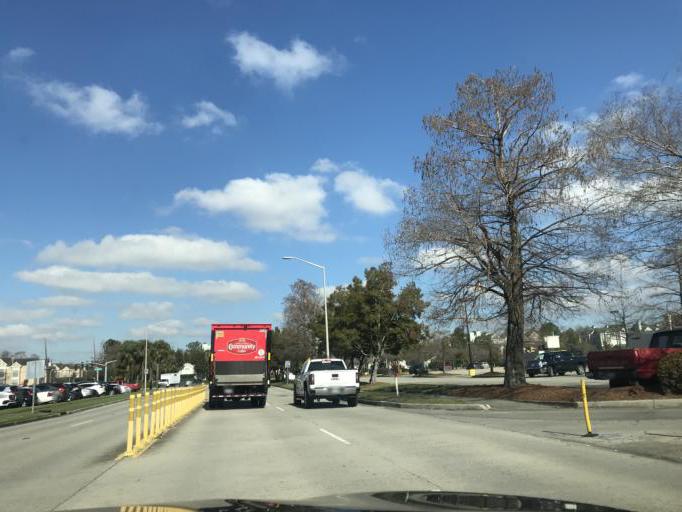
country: US
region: Louisiana
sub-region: Jefferson Parish
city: Elmwood
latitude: 29.9652
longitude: -90.1882
